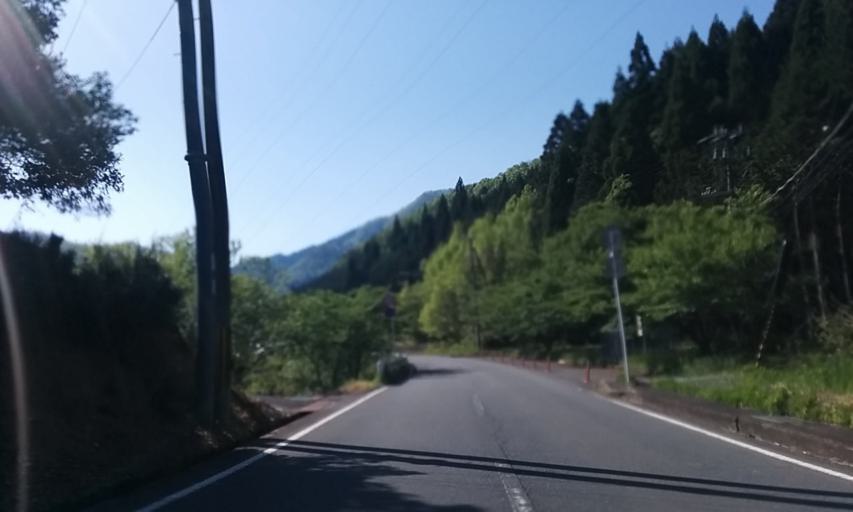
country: JP
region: Kyoto
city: Ayabe
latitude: 35.2630
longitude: 135.4408
